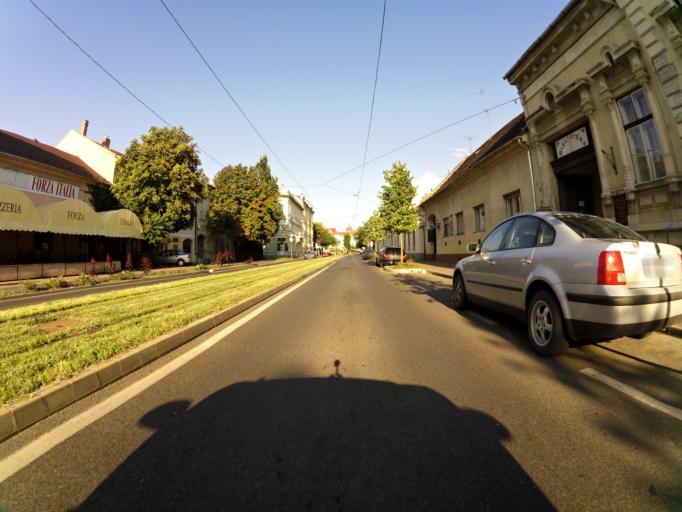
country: HU
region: Csongrad
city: Szeged
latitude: 46.2513
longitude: 20.1419
